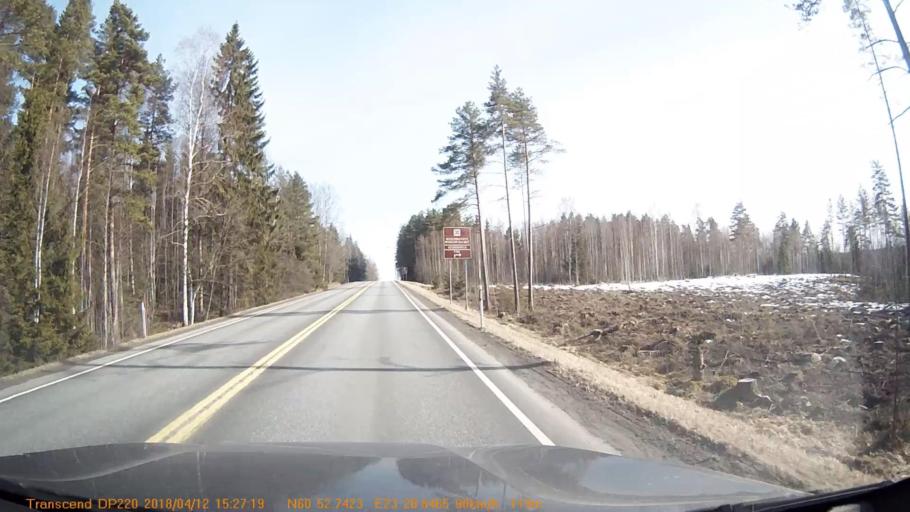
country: FI
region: Haeme
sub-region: Forssa
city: Jokioinen
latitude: 60.8784
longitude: 23.4821
